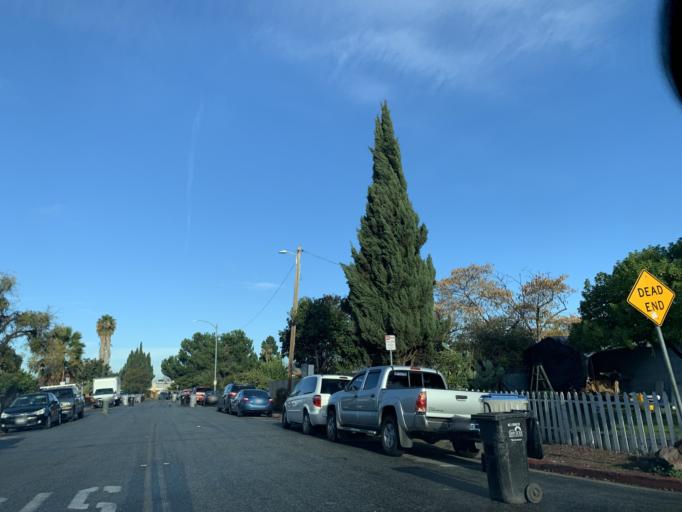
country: US
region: California
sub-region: Santa Clara County
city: Alum Rock
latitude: 37.3394
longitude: -121.8552
